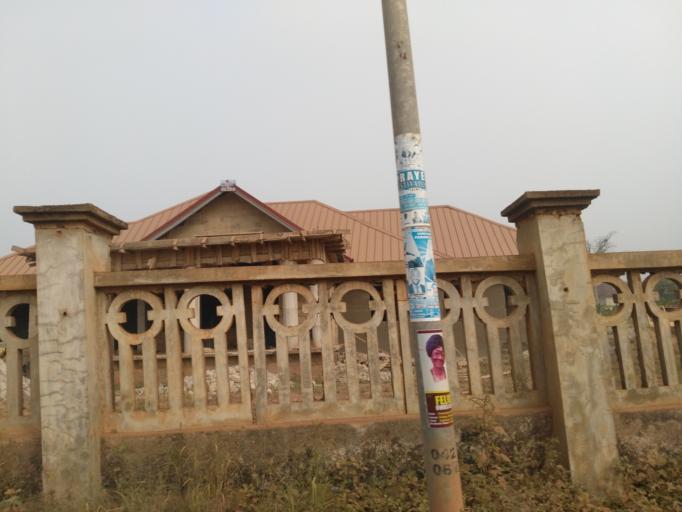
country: GH
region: Ashanti
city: Kumasi
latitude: 6.6520
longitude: -1.6232
